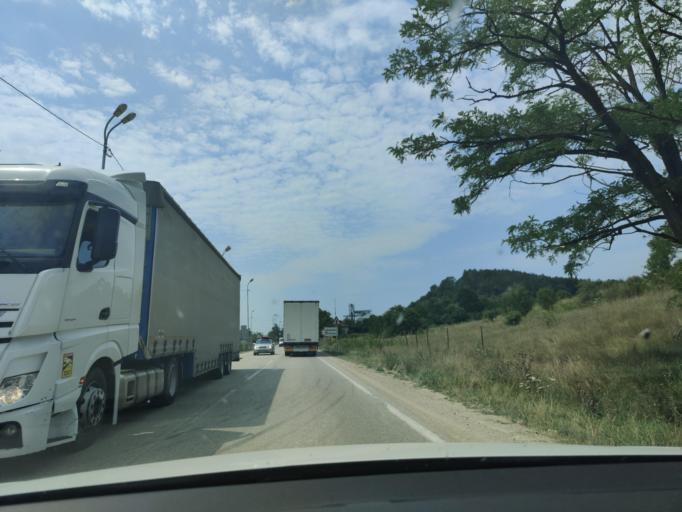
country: BG
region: Vidin
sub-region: Obshtina Dimovo
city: Dimovo
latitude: 43.7514
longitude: 22.7388
